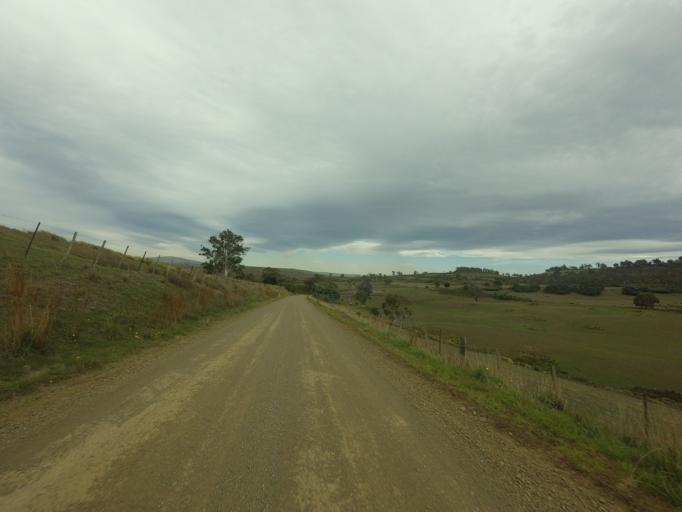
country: AU
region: Tasmania
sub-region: Derwent Valley
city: New Norfolk
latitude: -42.3986
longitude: 146.9472
